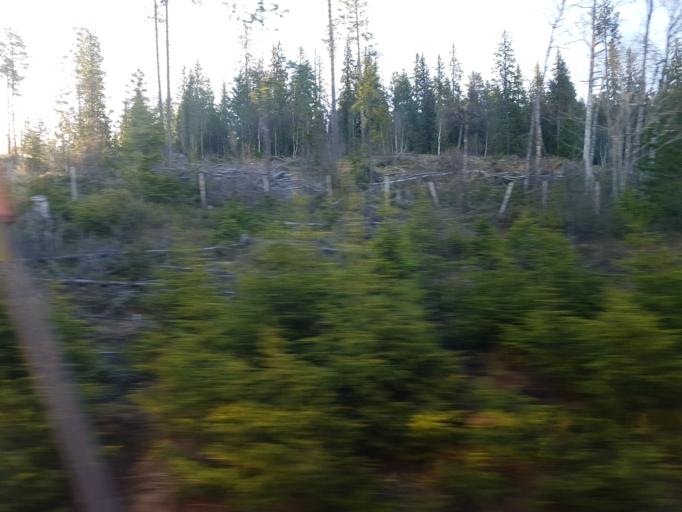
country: NO
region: Sor-Trondelag
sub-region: Rennebu
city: Berkak
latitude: 62.9201
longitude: 10.1474
